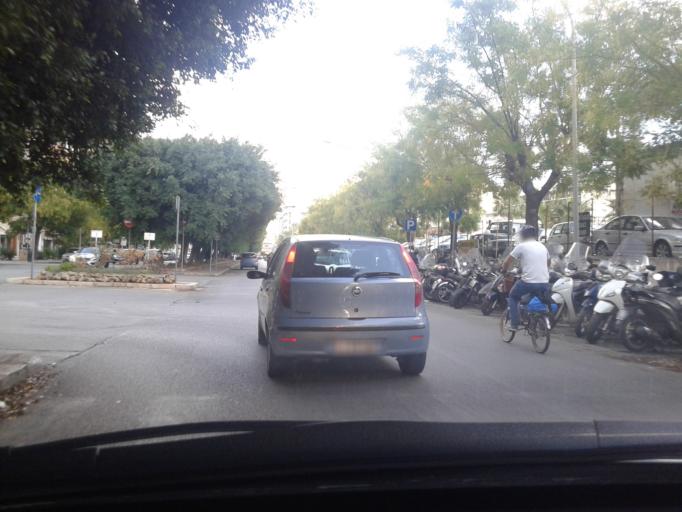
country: IT
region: Sicily
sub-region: Palermo
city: Palermo
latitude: 38.1508
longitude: 13.3298
